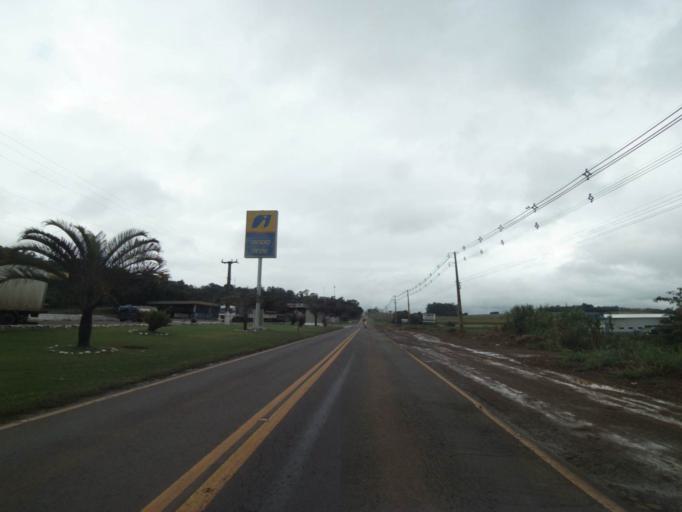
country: BR
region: Parana
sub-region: Marechal Candido Rondon
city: Marechal Candido Rondon
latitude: -24.5686
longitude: -54.0181
